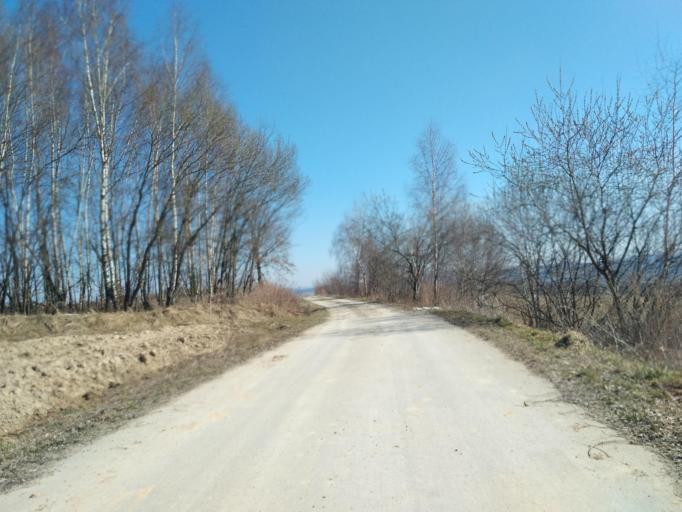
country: PL
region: Subcarpathian Voivodeship
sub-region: Powiat ropczycko-sedziszowski
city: Niedzwiada
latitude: 49.9550
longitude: 21.5540
